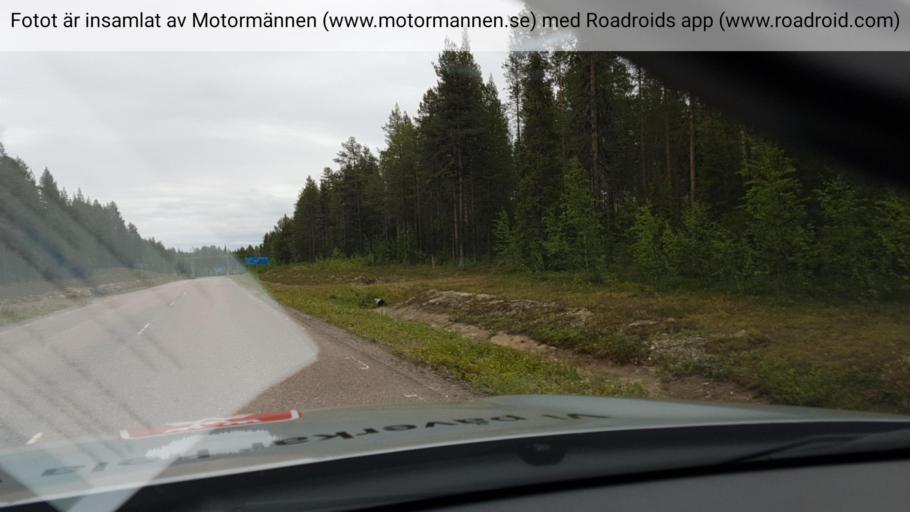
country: SE
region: Norrbotten
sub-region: Overkalix Kommun
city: OEverkalix
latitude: 67.0730
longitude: 22.5136
